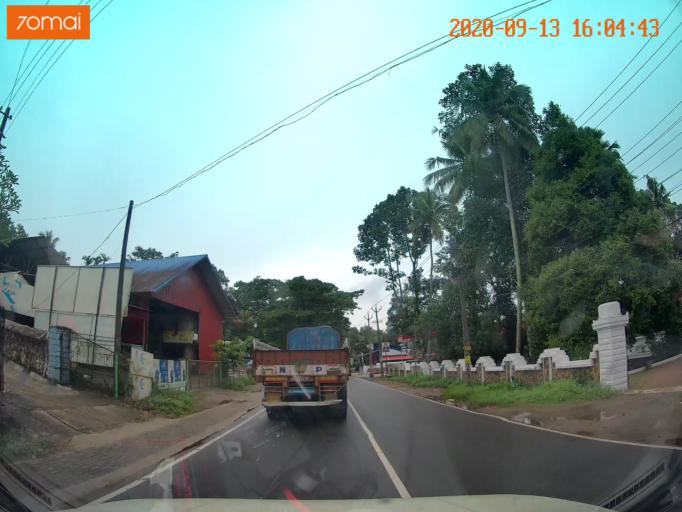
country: IN
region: Kerala
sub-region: Kottayam
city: Palackattumala
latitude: 9.6705
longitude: 76.5716
